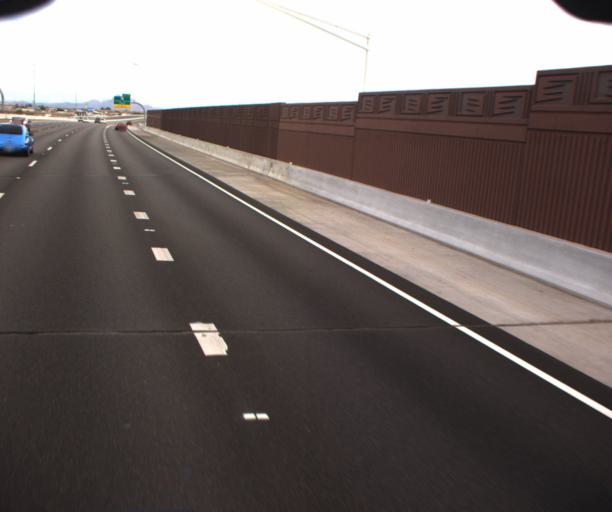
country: US
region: Arizona
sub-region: Maricopa County
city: Mesa
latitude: 33.4515
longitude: -111.8476
